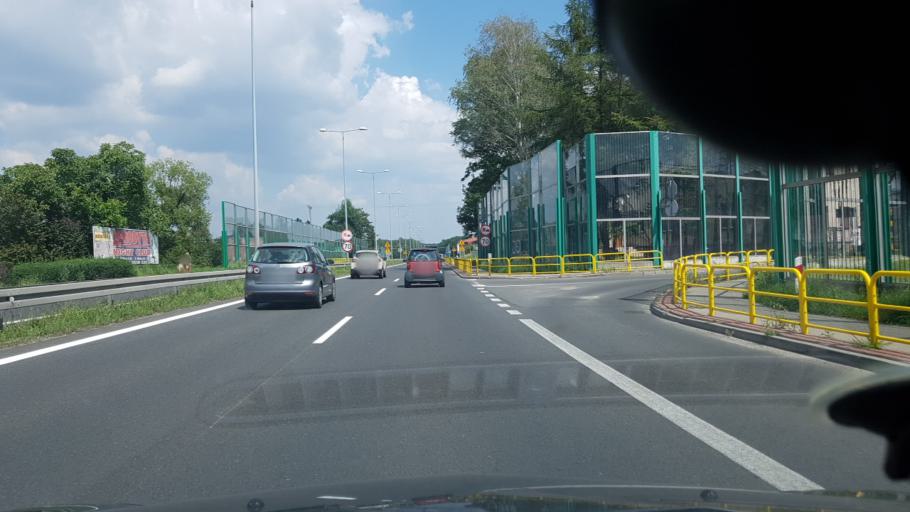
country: PL
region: Silesian Voivodeship
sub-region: Powiat mikolowski
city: Mikolow
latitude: 50.1903
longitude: 18.9221
